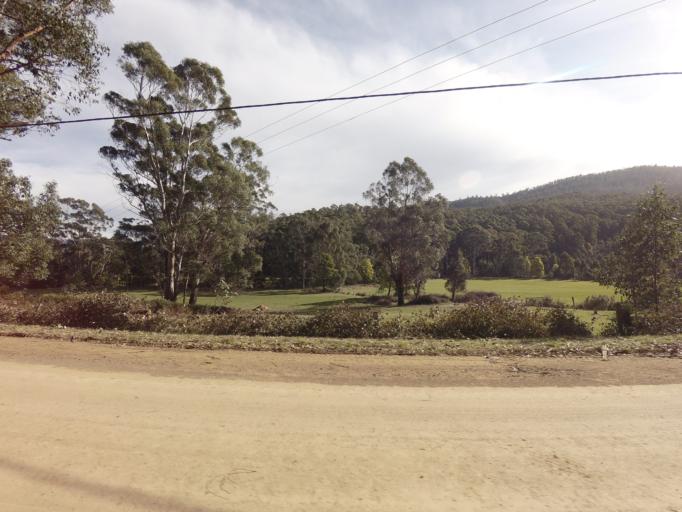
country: AU
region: Tasmania
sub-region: Huon Valley
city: Huonville
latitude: -43.0745
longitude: 147.0758
